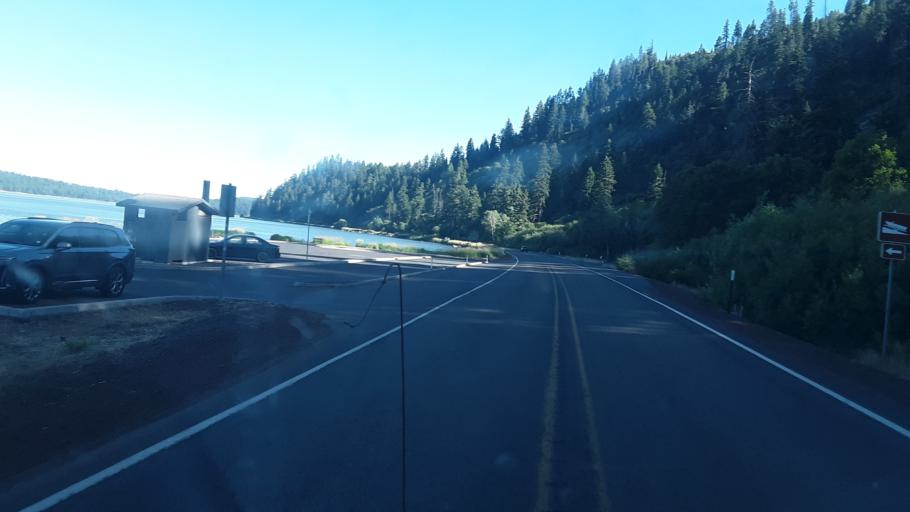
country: US
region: Oregon
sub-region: Klamath County
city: Klamath Falls
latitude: 42.3144
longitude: -121.9427
